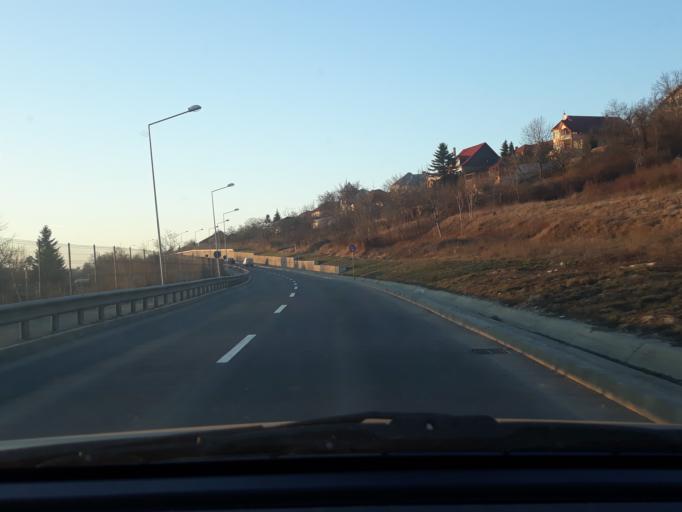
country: RO
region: Bihor
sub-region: Comuna Biharea
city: Oradea
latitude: 47.0587
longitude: 21.9474
